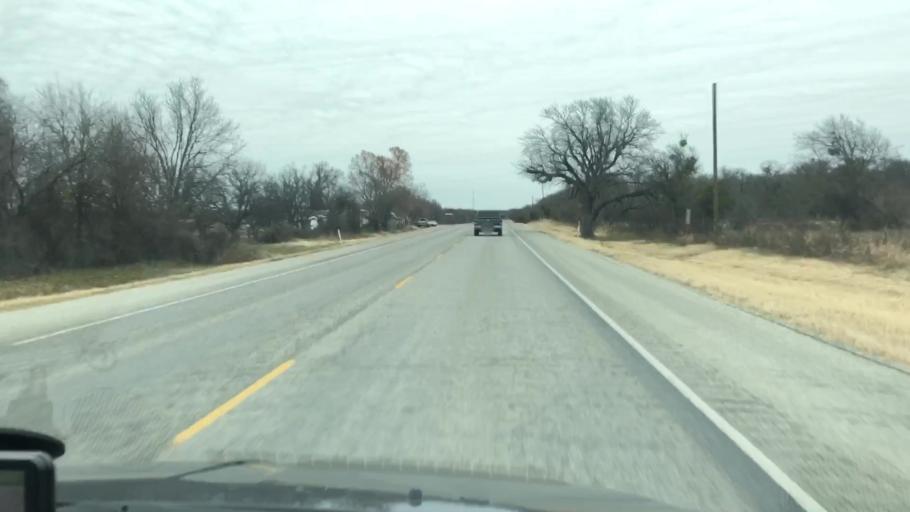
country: US
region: Texas
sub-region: Palo Pinto County
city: Mineral Wells
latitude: 32.8917
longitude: -98.0875
